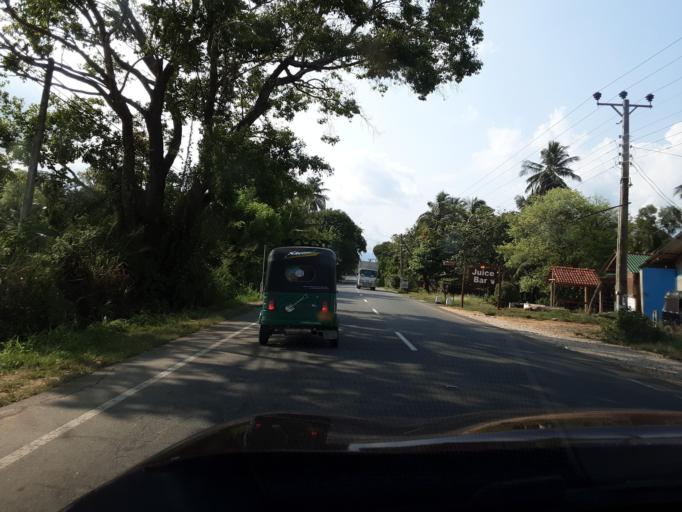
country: LK
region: Uva
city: Haputale
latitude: 6.5986
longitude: 81.1407
